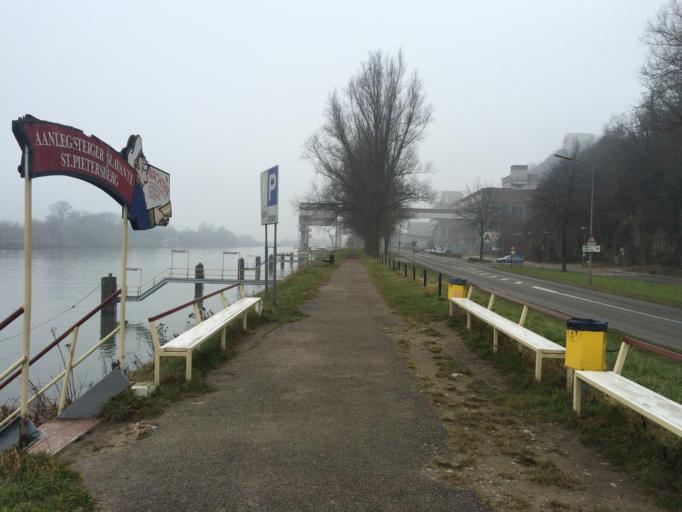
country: NL
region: Limburg
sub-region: Gemeente Maastricht
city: Maastricht
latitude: 50.8260
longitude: 5.6968
